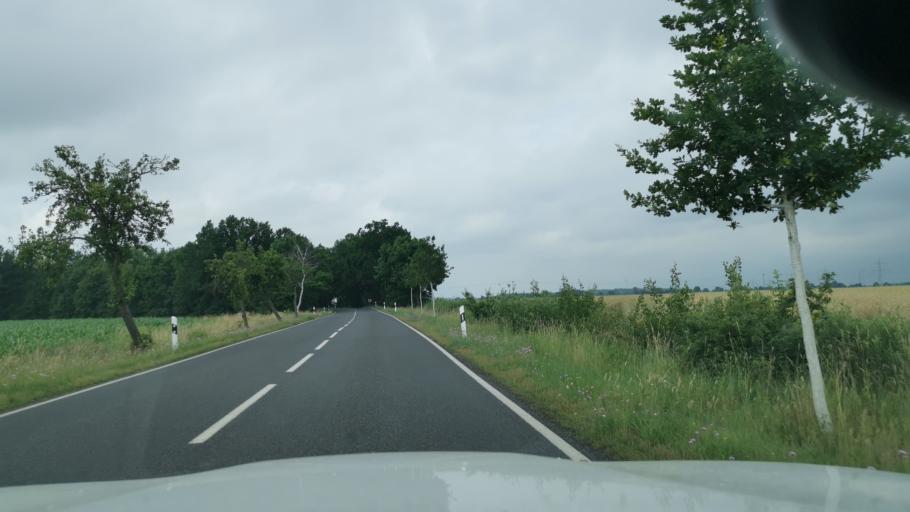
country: DE
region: Saxony-Anhalt
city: Annaburg
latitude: 51.7746
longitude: 13.0276
